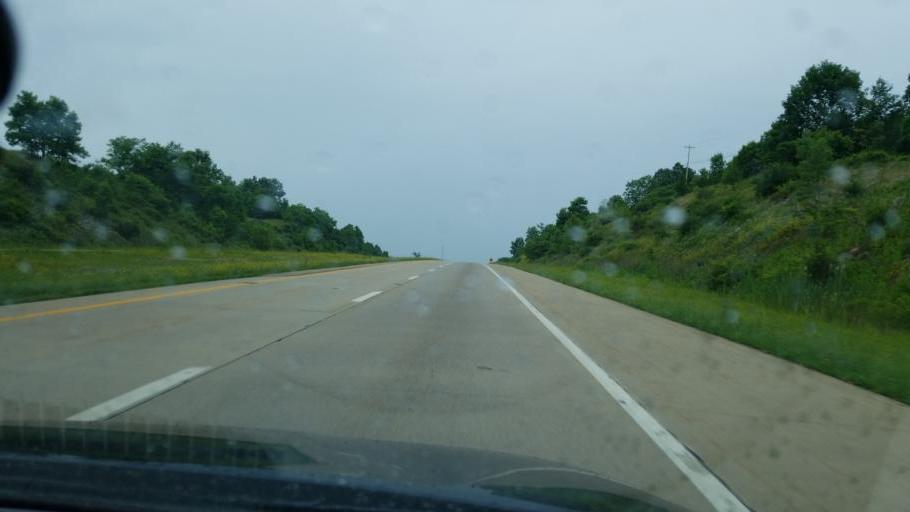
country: US
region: West Virginia
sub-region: Wood County
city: Washington
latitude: 39.2176
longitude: -81.8618
